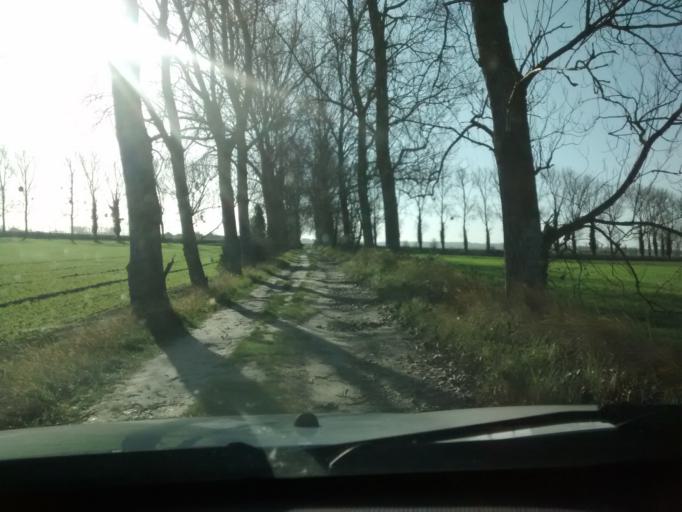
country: FR
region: Brittany
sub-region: Departement d'Ille-et-Vilaine
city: Roz-sur-Couesnon
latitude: 48.6288
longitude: -1.5340
